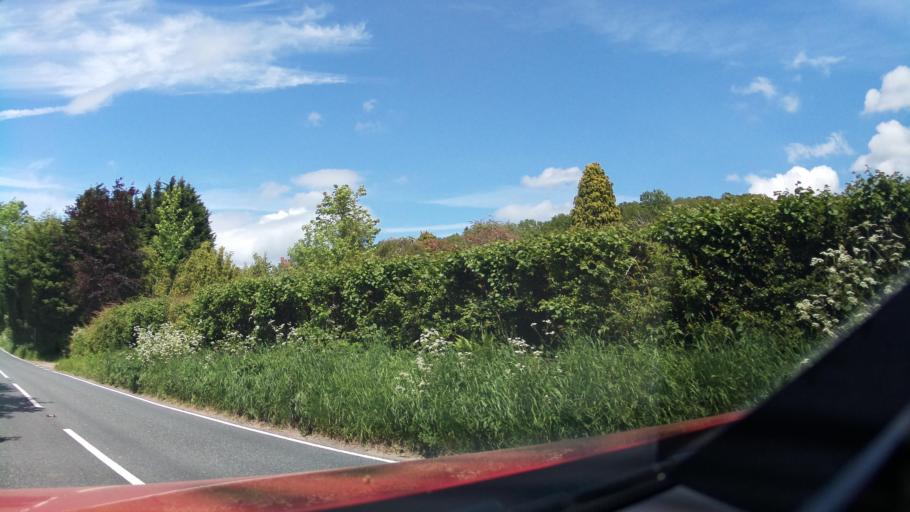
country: GB
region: Wales
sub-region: Monmouthshire
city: Mitchel Troy
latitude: 51.7557
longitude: -2.7221
